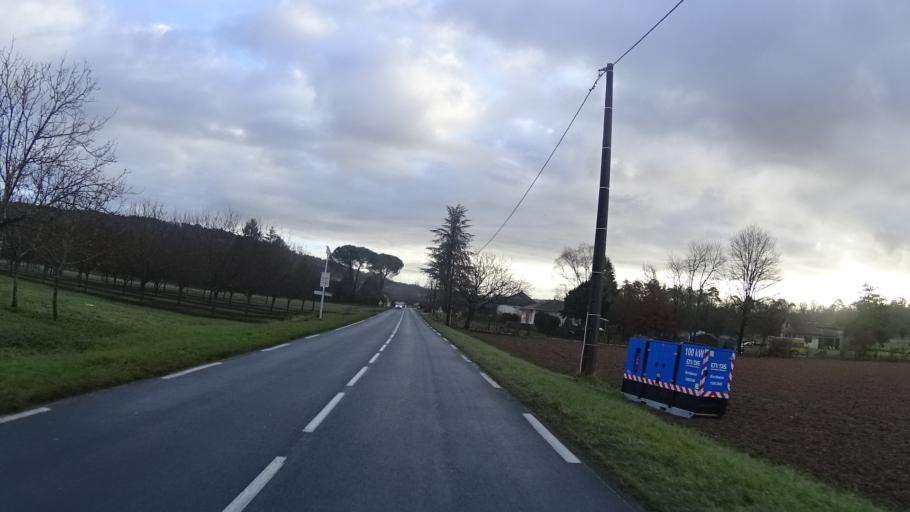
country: FR
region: Aquitaine
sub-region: Departement de la Dordogne
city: Antonne-et-Trigonant
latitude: 45.1909
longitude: 0.8393
